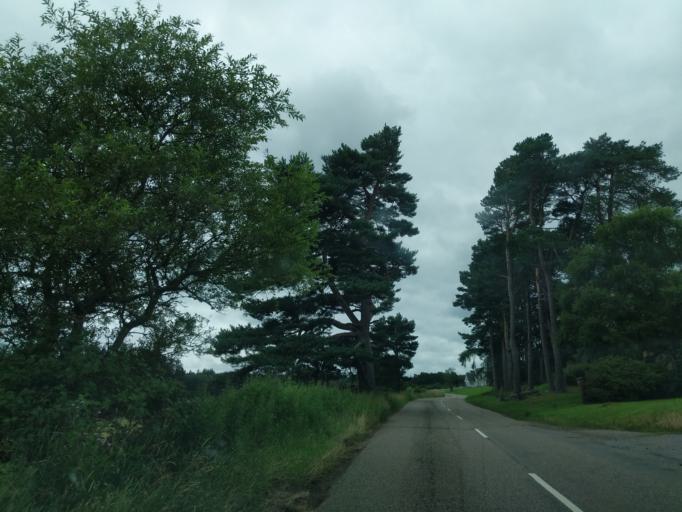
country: GB
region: Scotland
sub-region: Moray
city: Rothes
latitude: 57.4867
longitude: -3.2491
